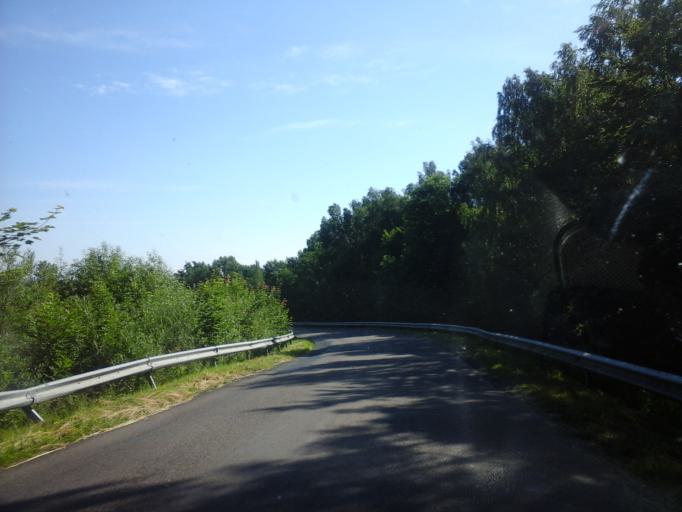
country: PL
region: West Pomeranian Voivodeship
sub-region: Powiat swidwinski
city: Polczyn-Zdroj
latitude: 53.7399
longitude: 16.0815
